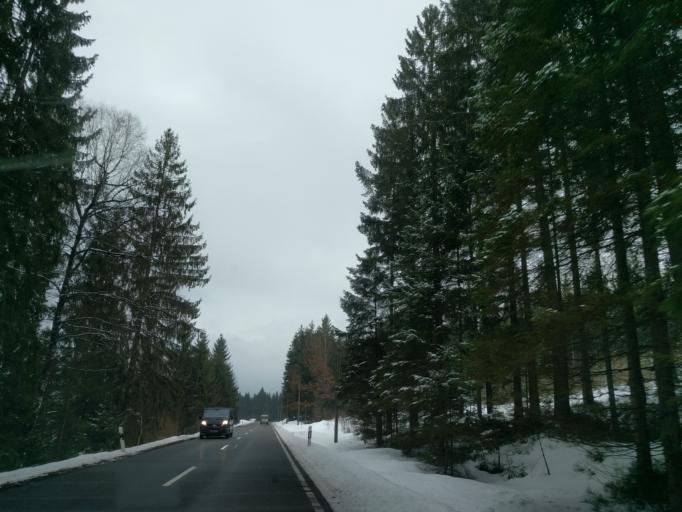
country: DE
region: Bavaria
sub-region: Lower Bavaria
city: Lindberg
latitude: 49.0502
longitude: 13.2465
